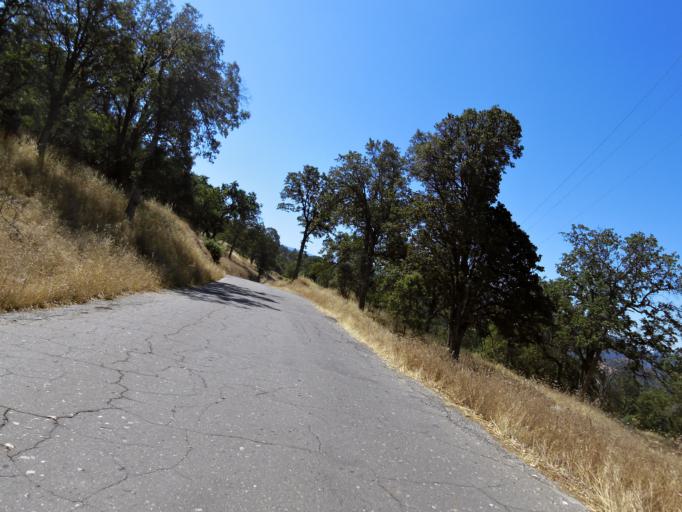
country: US
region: California
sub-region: Fresno County
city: Auberry
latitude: 37.1829
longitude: -119.4621
